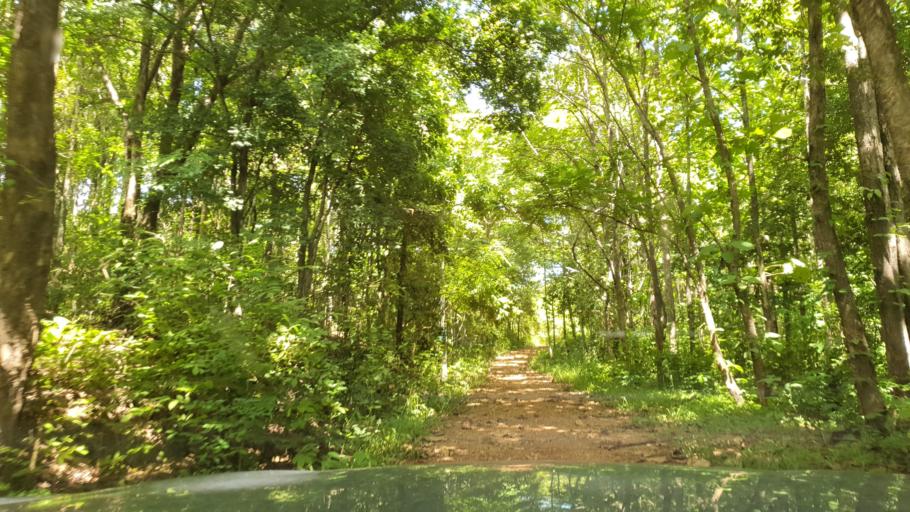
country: TH
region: Chiang Mai
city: Mae On
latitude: 18.7335
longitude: 99.2374
